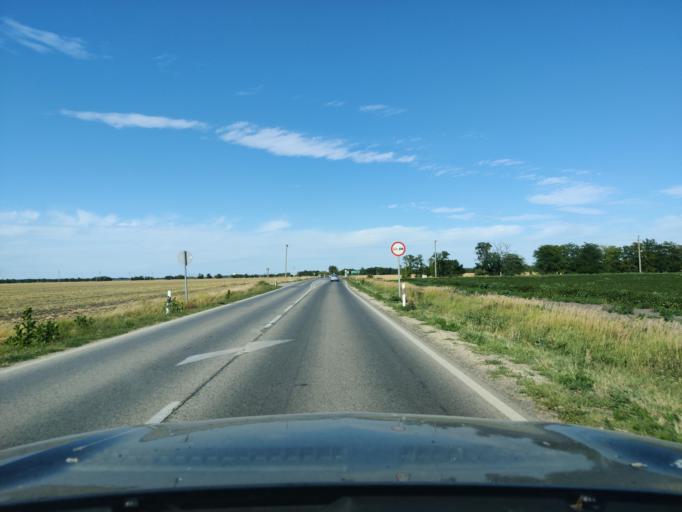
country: HU
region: Gyor-Moson-Sopron
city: Janossomorja
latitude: 47.8202
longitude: 17.1935
